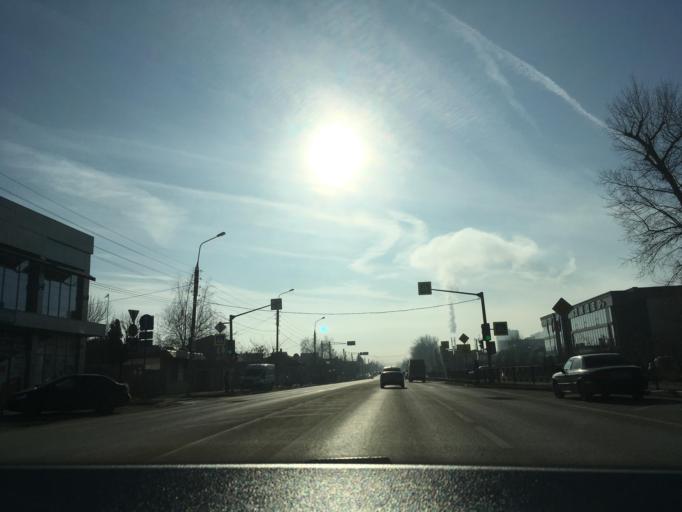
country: RU
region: Krasnodarskiy
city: Krasnodar
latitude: 45.1003
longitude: 39.0131
